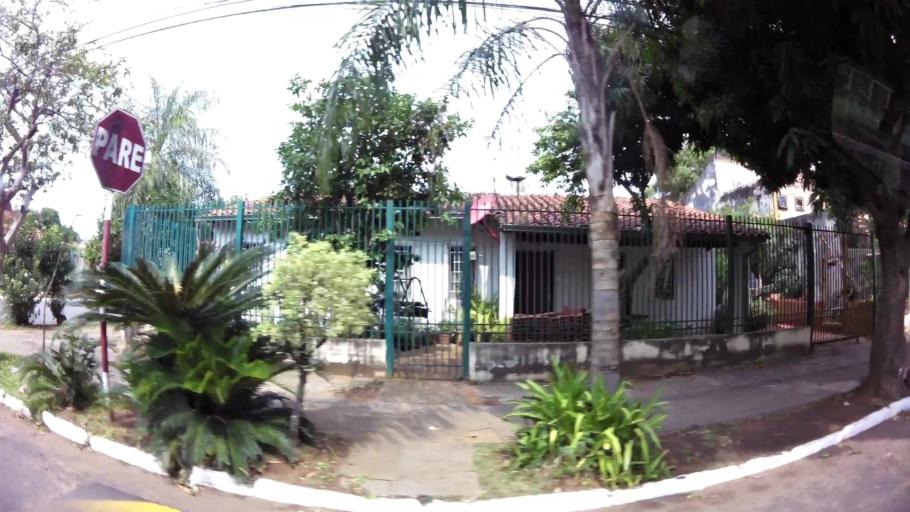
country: PY
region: Asuncion
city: Asuncion
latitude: -25.2733
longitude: -57.5635
